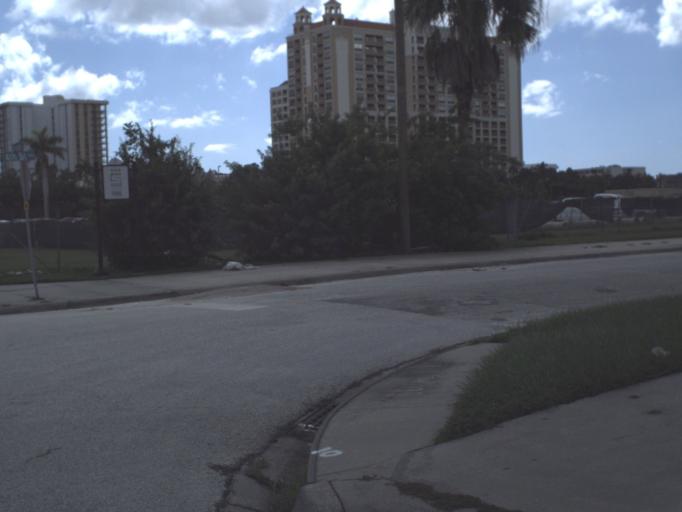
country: US
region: Florida
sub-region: Sarasota County
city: Sarasota
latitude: 27.3399
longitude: -82.5469
